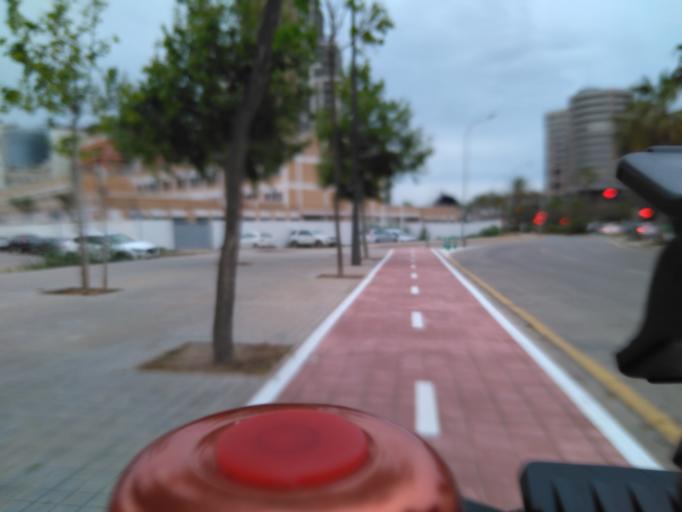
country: ES
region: Valencia
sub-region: Provincia de Valencia
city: Mislata
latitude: 39.4889
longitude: -0.4030
